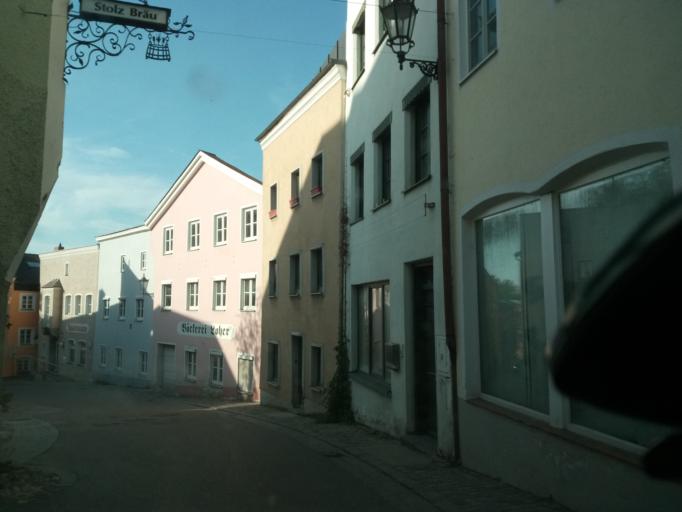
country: DE
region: Bavaria
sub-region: Upper Bavaria
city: Kraiburg am Inn
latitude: 48.1825
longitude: 12.4283
